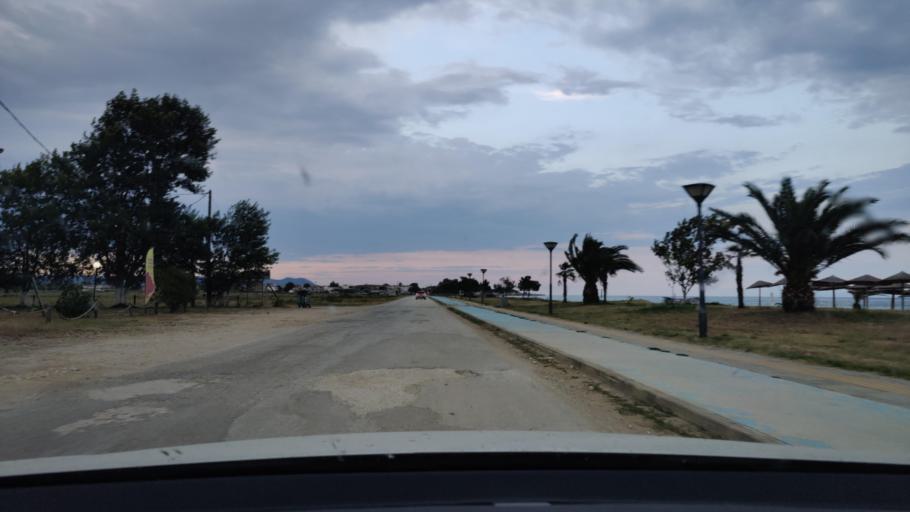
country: GR
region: East Macedonia and Thrace
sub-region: Nomos Kavalas
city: Paralia Ofryniou
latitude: 40.7692
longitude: 23.8917
